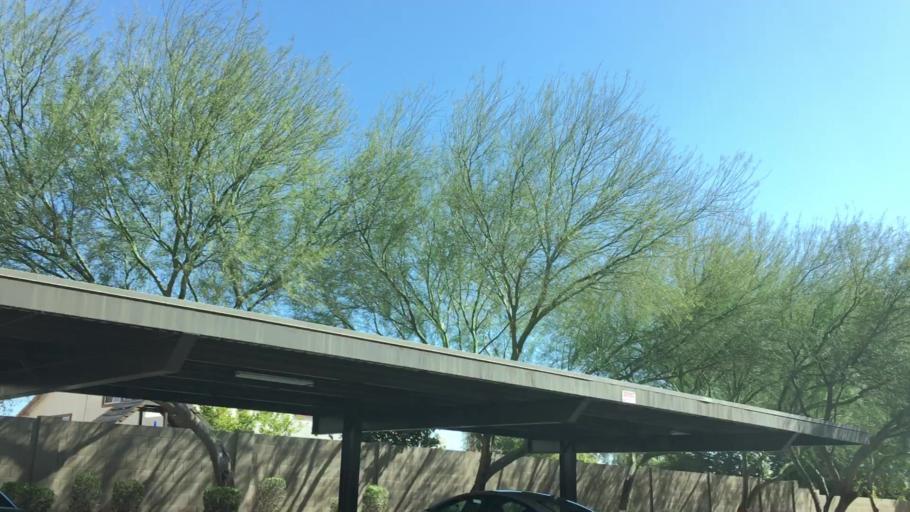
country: US
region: Arizona
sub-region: Maricopa County
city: Peoria
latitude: 33.6130
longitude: -112.2333
